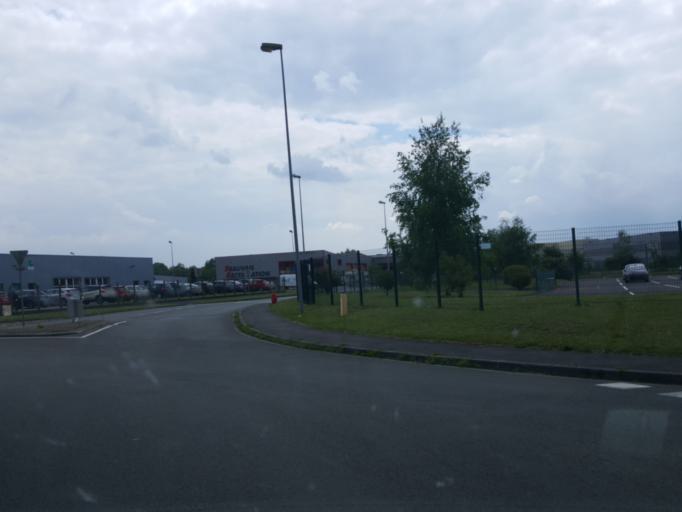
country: FR
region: Picardie
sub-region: Departement de l'Oise
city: Allonne
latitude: 49.4154
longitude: 2.1293
